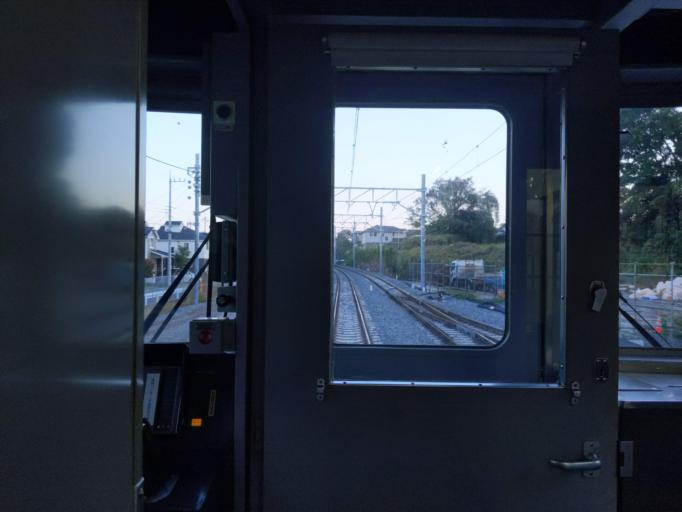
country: JP
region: Chiba
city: Noda
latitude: 35.9579
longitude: 139.8607
